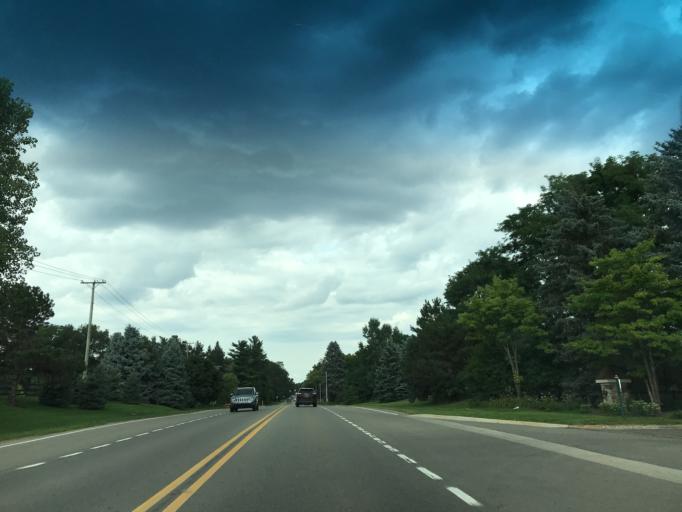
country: US
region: Michigan
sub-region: Oakland County
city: Milford
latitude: 42.5525
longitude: -83.6179
